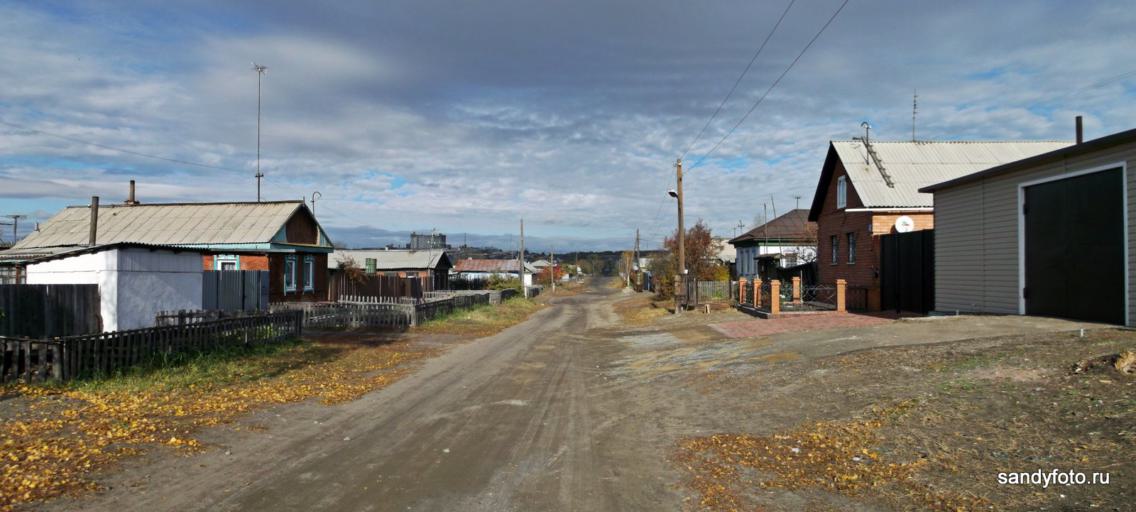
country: RU
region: Chelyabinsk
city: Troitsk
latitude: 54.0907
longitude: 61.5924
